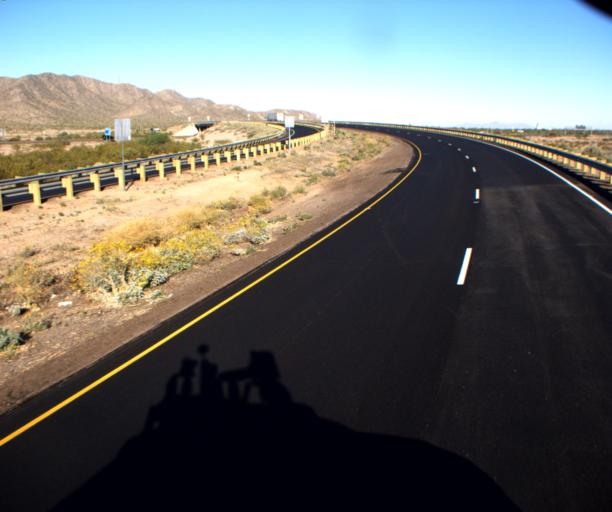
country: US
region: Arizona
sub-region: Pinal County
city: Arizona City
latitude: 32.8185
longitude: -111.6801
